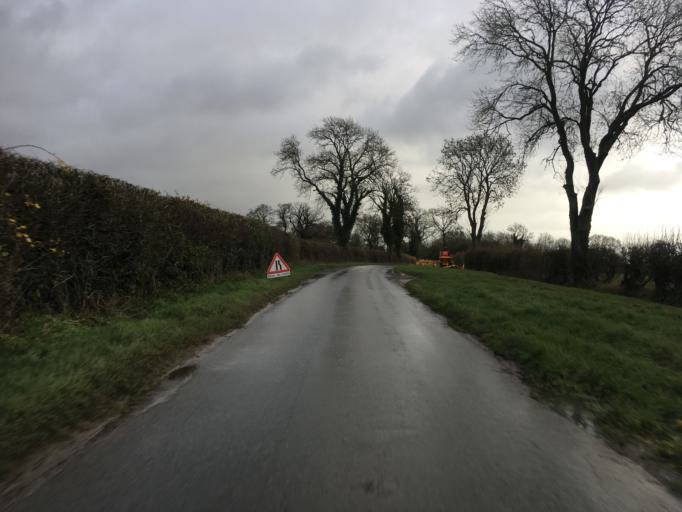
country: GB
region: England
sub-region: Wiltshire
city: Charlton
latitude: 51.6354
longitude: -2.0946
